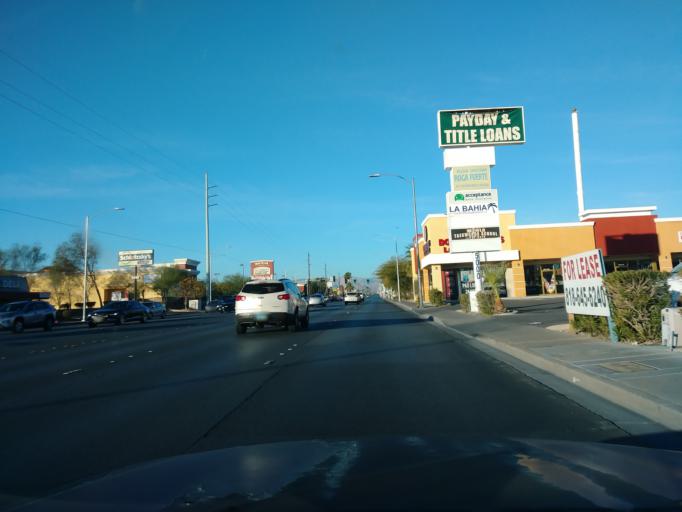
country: US
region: Nevada
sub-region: Clark County
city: Spring Valley
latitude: 36.1592
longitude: -115.2085
